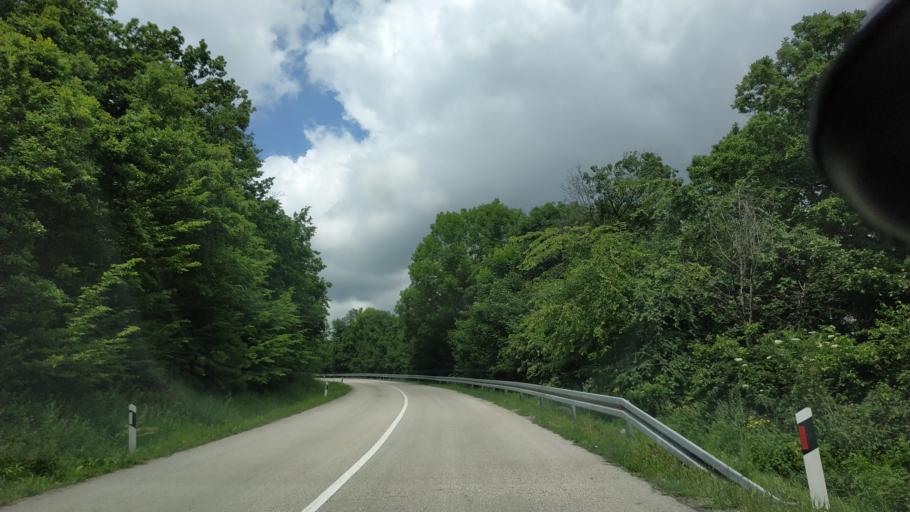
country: RS
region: Central Serbia
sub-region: Borski Okrug
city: Bor
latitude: 44.0824
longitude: 22.0149
